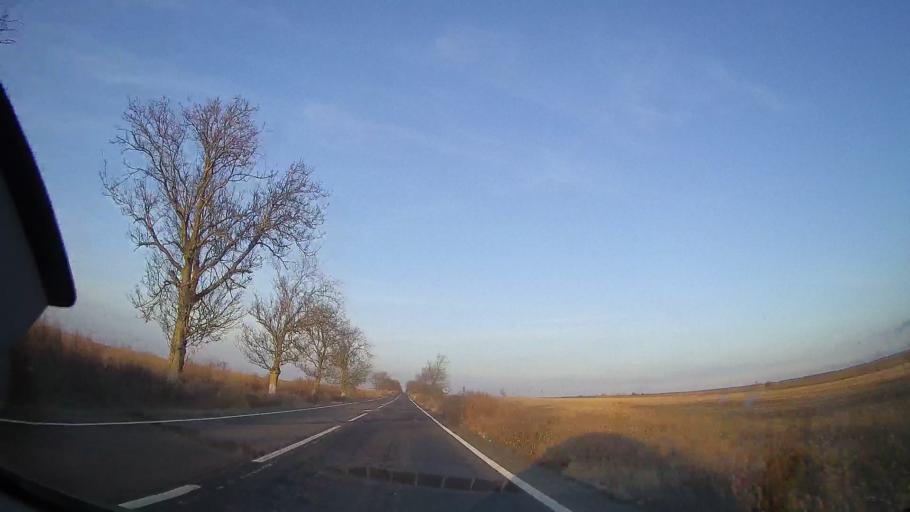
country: RO
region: Constanta
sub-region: Comuna Amzacea
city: Amzacea
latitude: 43.9354
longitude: 28.3649
